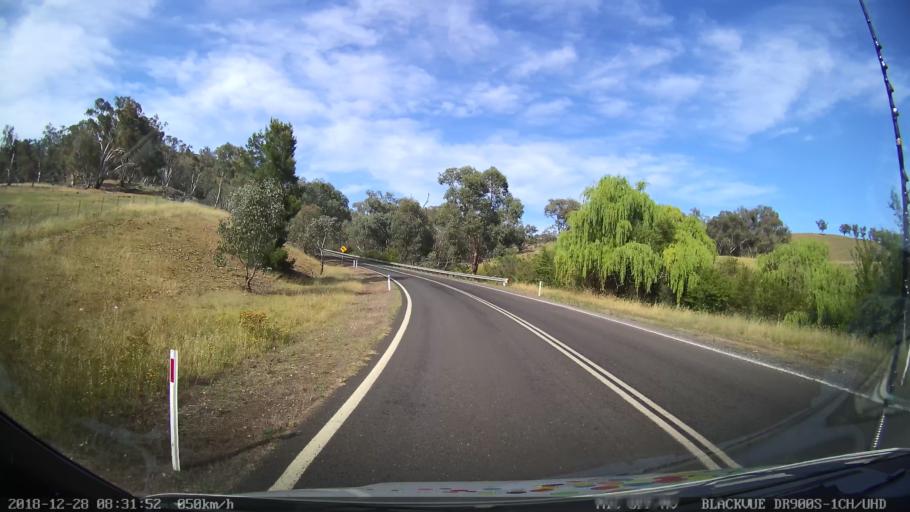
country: AU
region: New South Wales
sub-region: Blayney
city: Blayney
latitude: -33.9612
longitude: 149.3159
